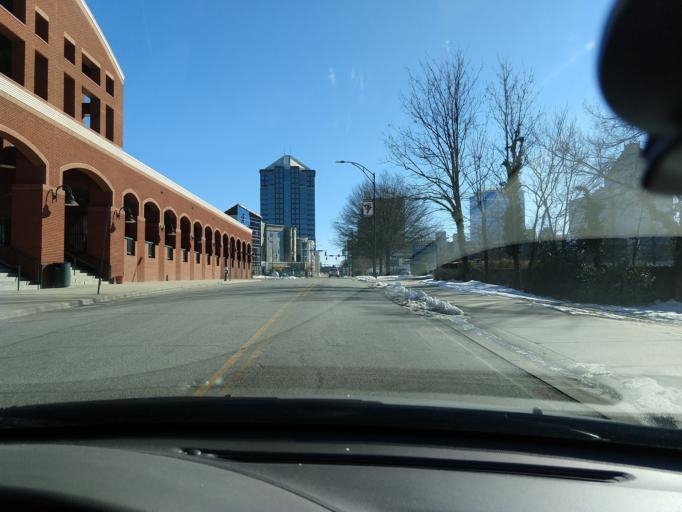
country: US
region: North Carolina
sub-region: Guilford County
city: Greensboro
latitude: 36.0757
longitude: -79.7954
